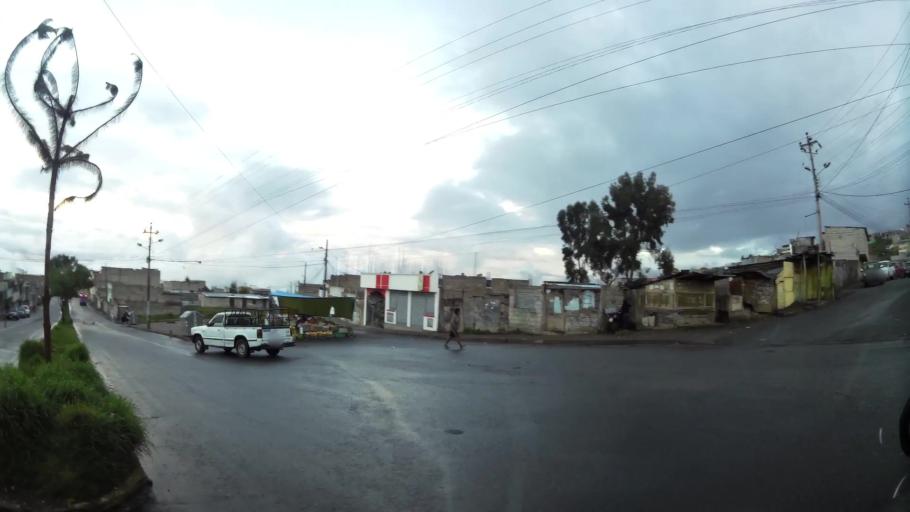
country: EC
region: Pichincha
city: Quito
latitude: -0.0914
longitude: -78.5249
